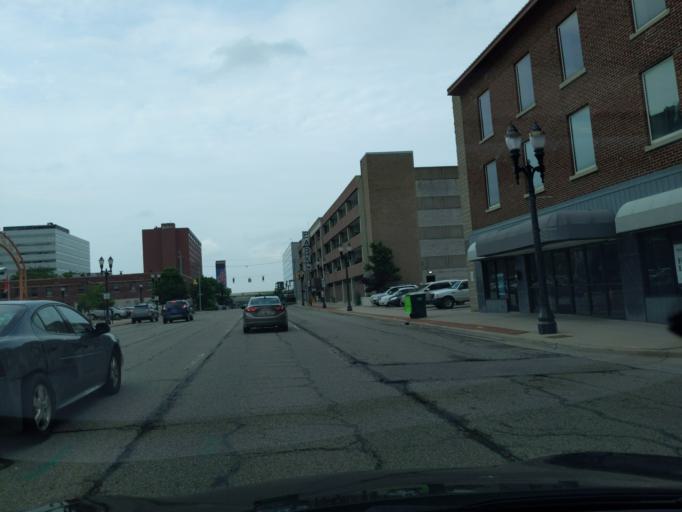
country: US
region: Michigan
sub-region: Ingham County
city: Lansing
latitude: 42.7316
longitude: -84.5507
